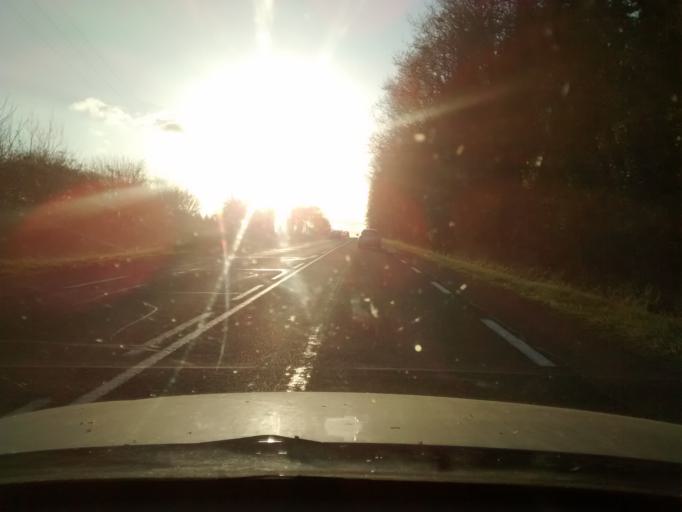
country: FR
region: Pays de la Loire
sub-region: Departement de la Sarthe
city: Brulon
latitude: 48.0229
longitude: -0.2263
